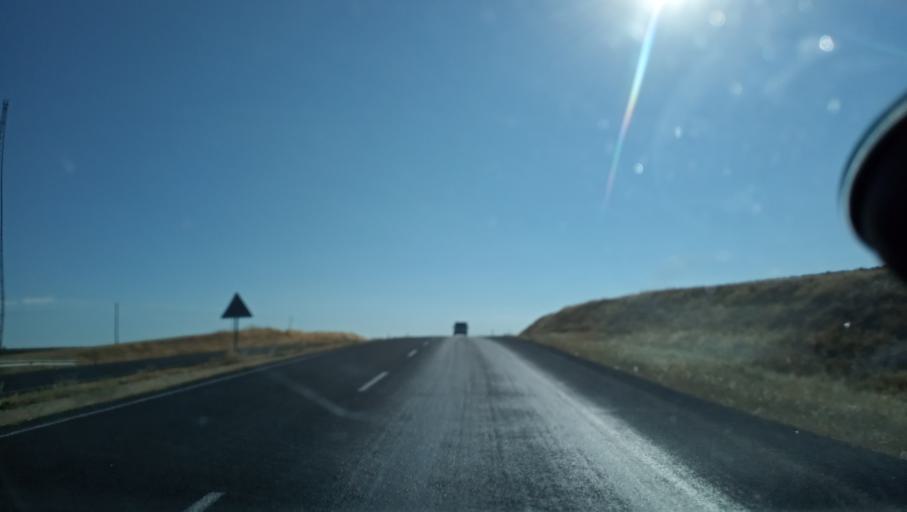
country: TR
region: Diyarbakir
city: Sur
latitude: 37.9938
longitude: 40.4000
